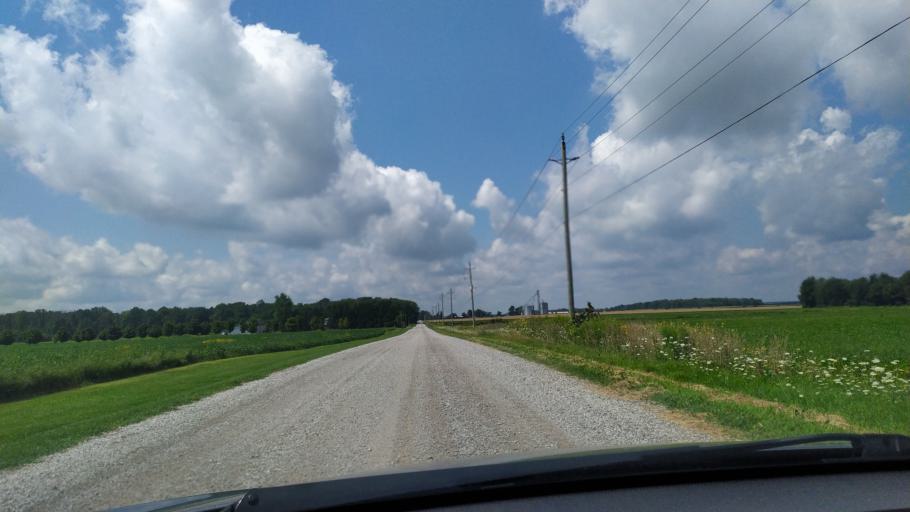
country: CA
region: Ontario
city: London
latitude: 43.0813
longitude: -81.3270
